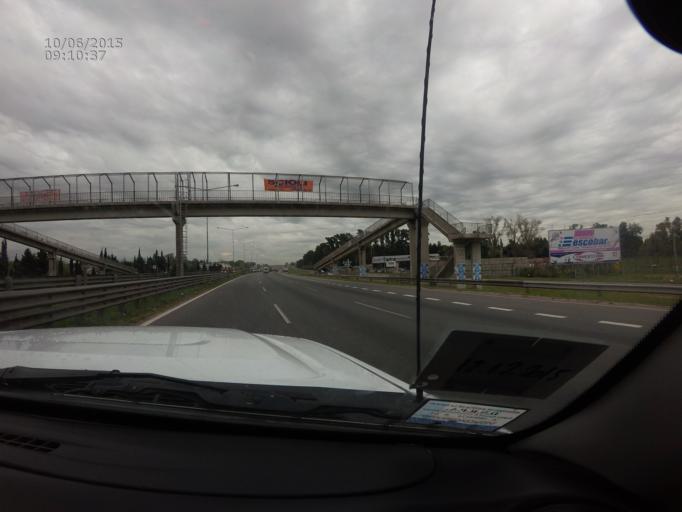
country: AR
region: Buenos Aires
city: Belen de Escobar
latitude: -34.3692
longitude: -58.7755
